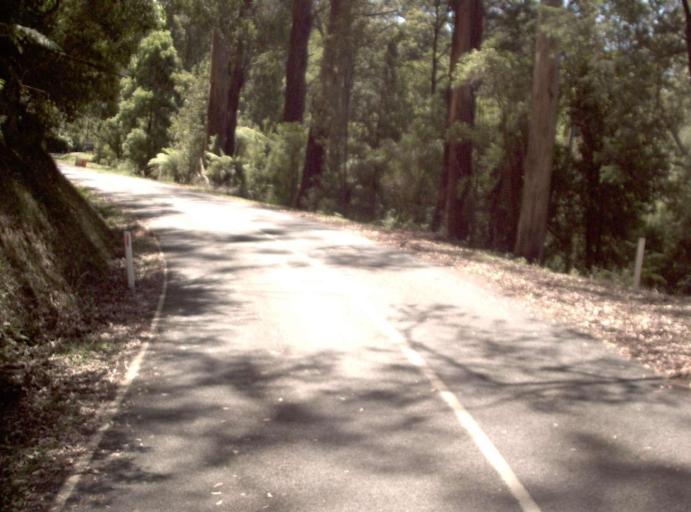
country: AU
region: Victoria
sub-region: Yarra Ranges
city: Millgrove
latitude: -37.7348
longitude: 145.7216
